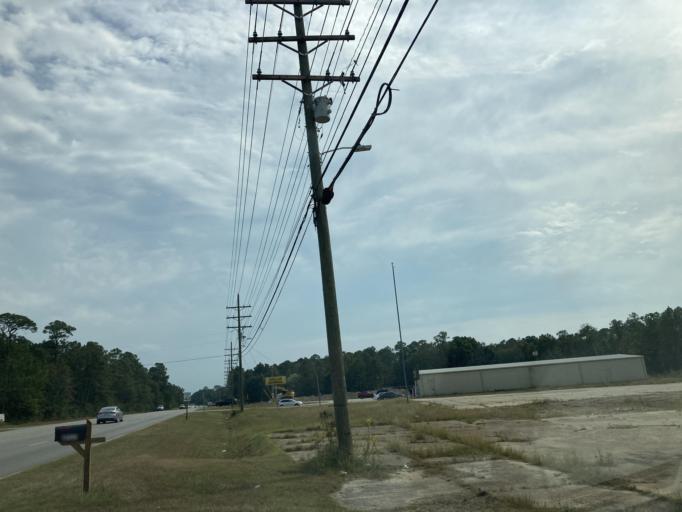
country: US
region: Mississippi
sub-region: Jackson County
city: Saint Martin
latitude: 30.4692
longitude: -88.8482
